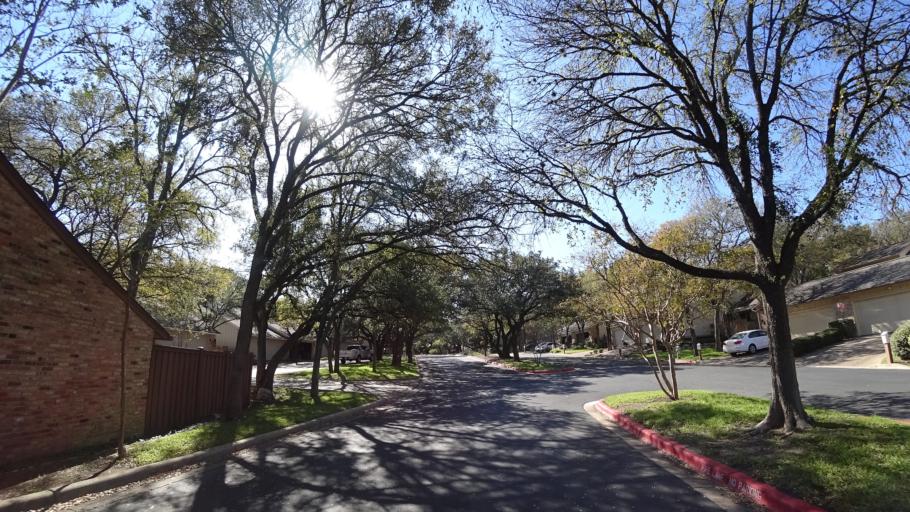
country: US
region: Texas
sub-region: Williamson County
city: Jollyville
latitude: 30.3734
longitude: -97.7472
